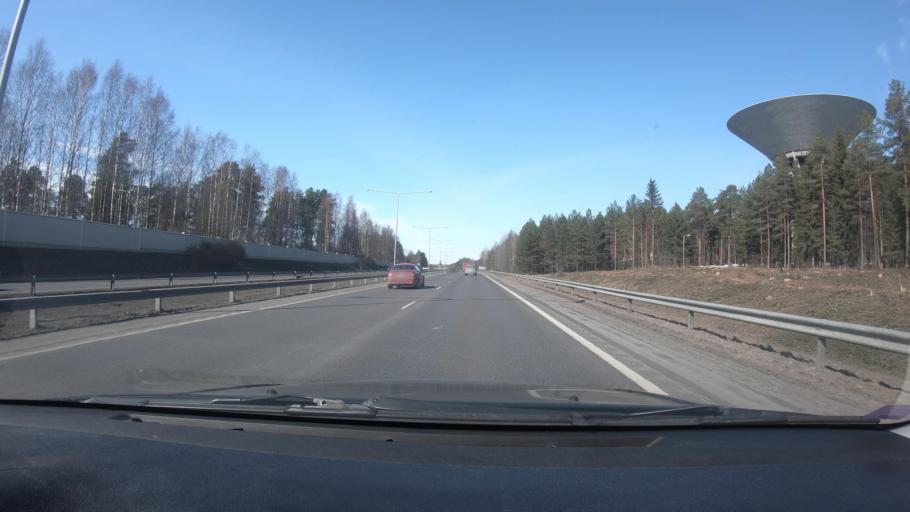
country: FI
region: Northern Ostrobothnia
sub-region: Oulu
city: Oulu
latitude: 65.0359
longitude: 25.4864
